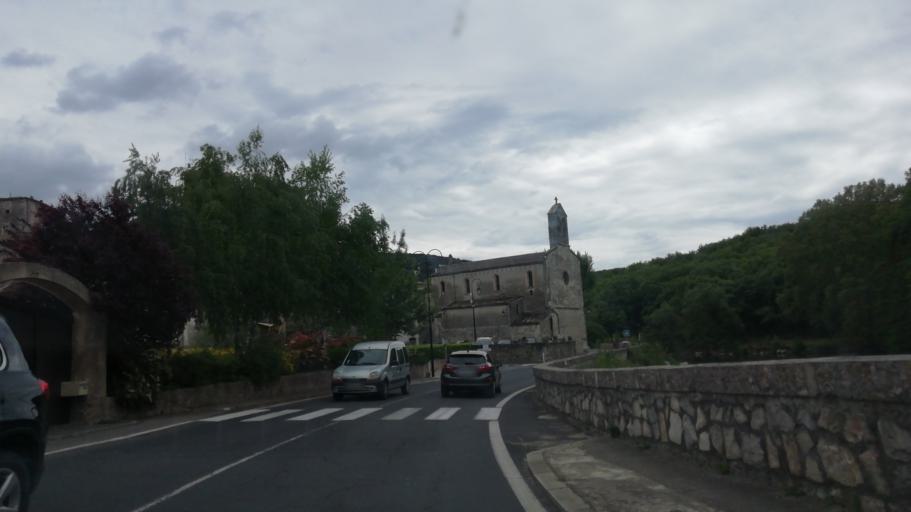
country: FR
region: Languedoc-Roussillon
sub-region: Departement de l'Herault
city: Laroque
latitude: 43.9233
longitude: 3.7226
